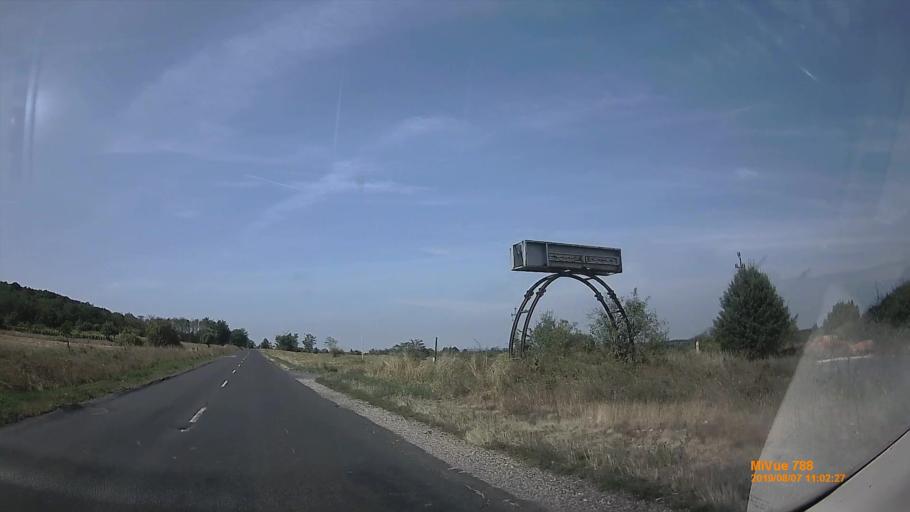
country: HU
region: Veszprem
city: Ajka
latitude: 47.0301
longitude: 17.5251
